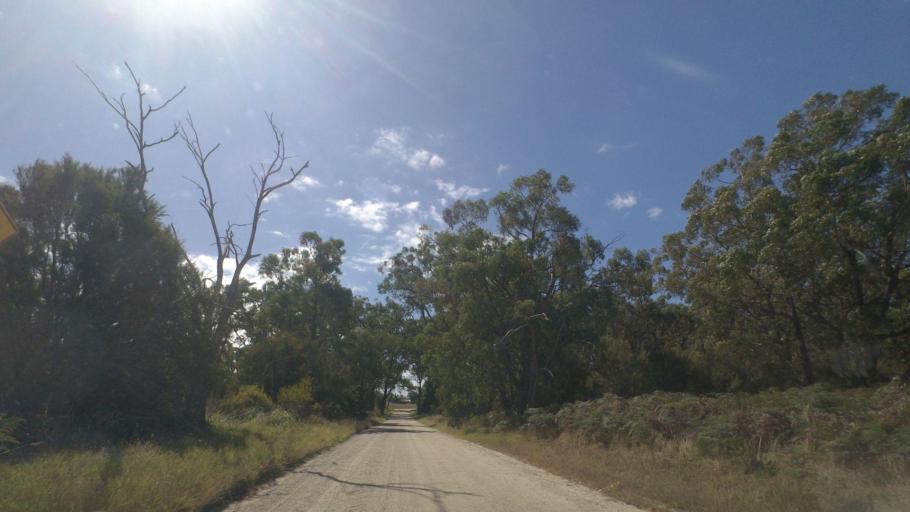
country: AU
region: Victoria
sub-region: Cardinia
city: Bunyip
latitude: -38.2775
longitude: 145.6620
